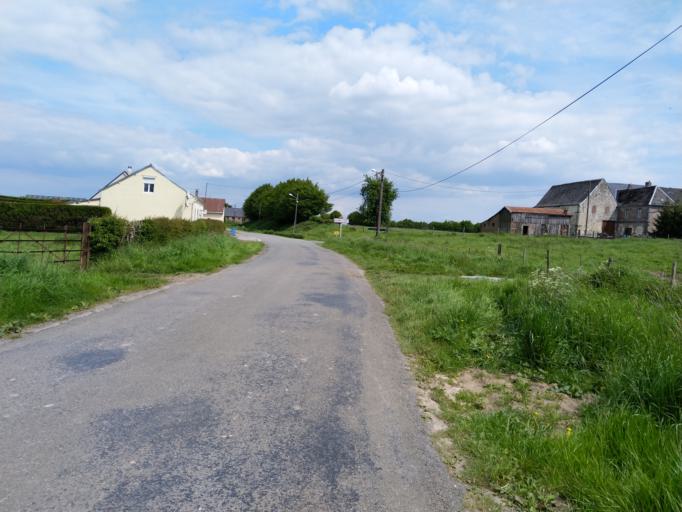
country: FR
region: Picardie
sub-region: Departement de l'Aisne
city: Boue
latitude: 50.0414
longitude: 3.6663
